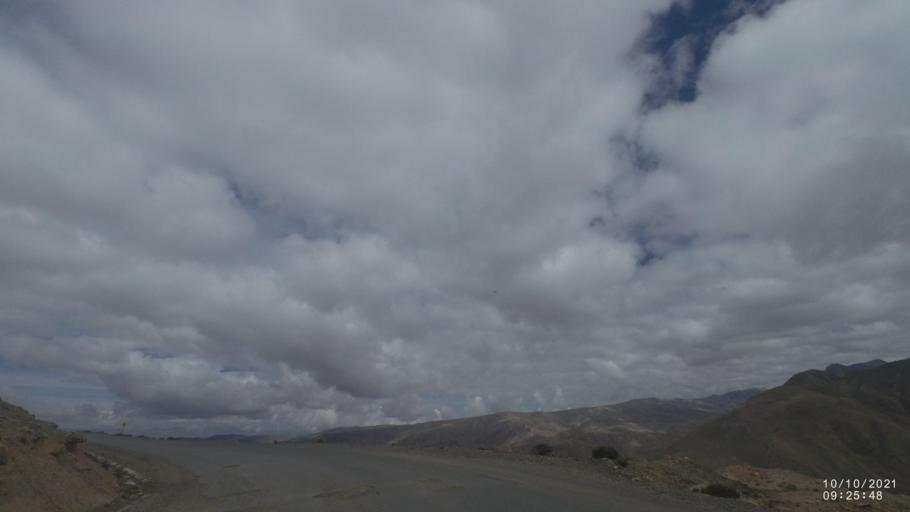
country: BO
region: La Paz
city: Quime
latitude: -17.0929
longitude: -67.3178
